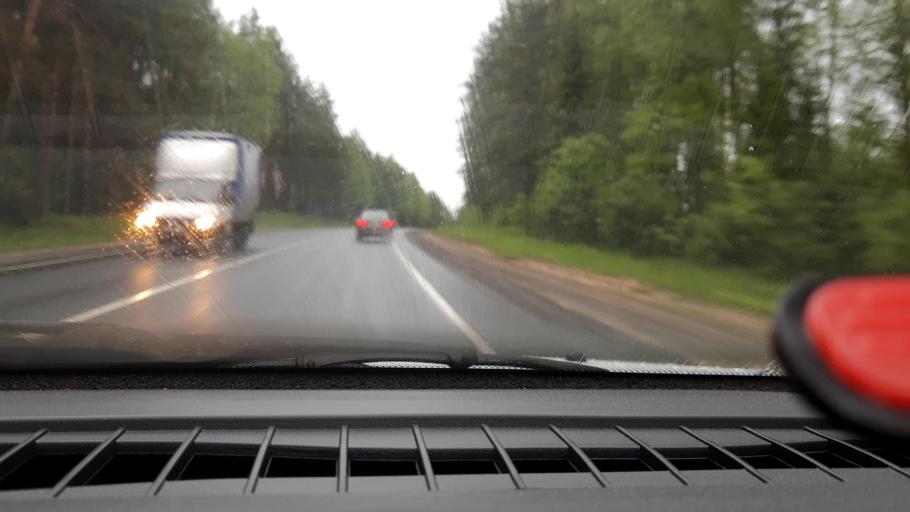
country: RU
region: Nizjnij Novgorod
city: Linda
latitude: 56.7189
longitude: 44.2744
